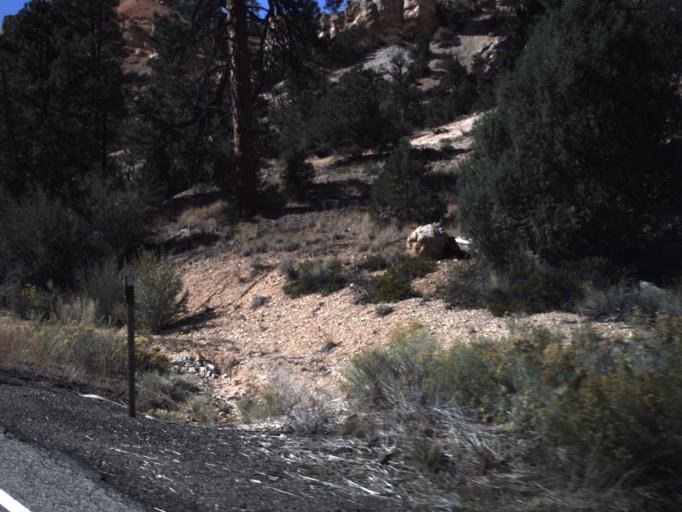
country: US
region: Utah
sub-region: Garfield County
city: Panguitch
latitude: 37.6839
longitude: -112.1210
